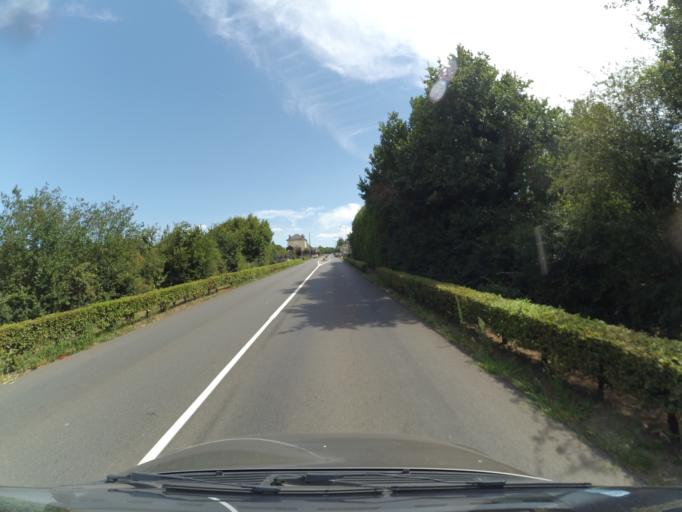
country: FR
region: Poitou-Charentes
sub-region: Departement de la Charente
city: Confolens
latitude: 45.9659
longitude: 0.6973
